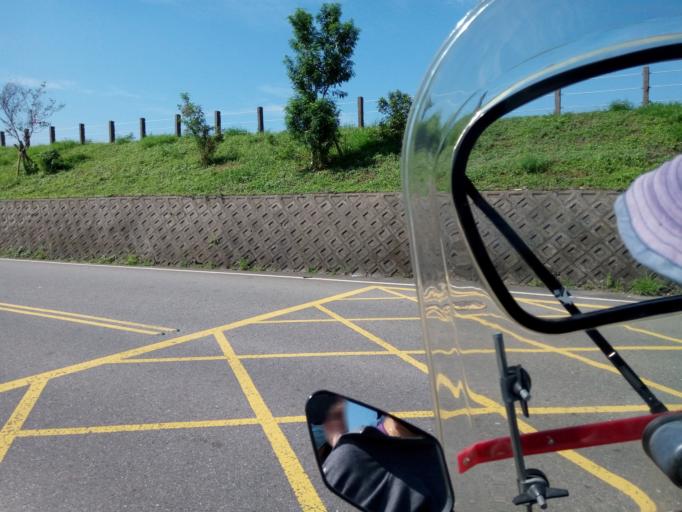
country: TW
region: Taiwan
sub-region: Yilan
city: Yilan
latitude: 24.6763
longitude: 121.7442
